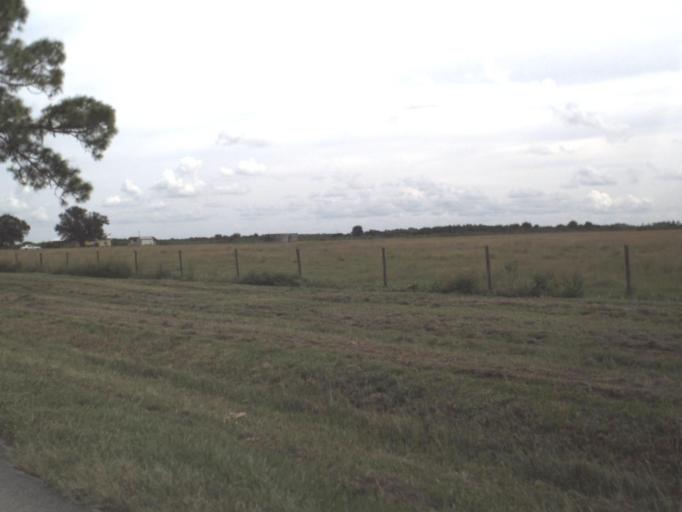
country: US
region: Florida
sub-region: Okeechobee County
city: Taylor Creek
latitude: 27.2818
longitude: -80.7100
